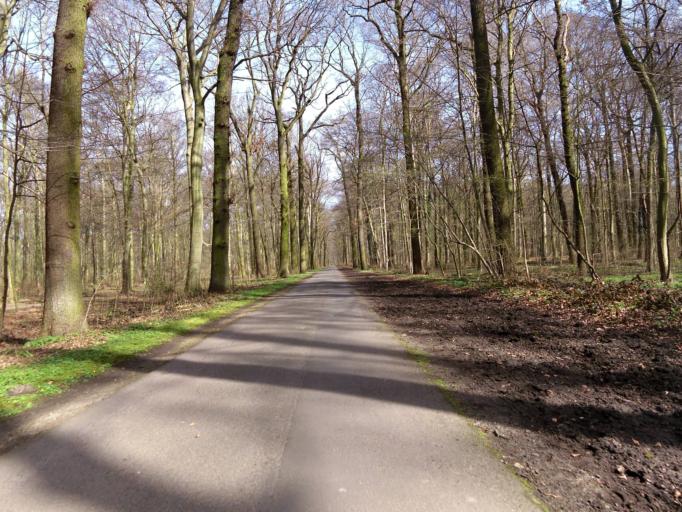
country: DE
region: Lower Saxony
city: Laatzen
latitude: 52.3533
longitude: 9.7759
